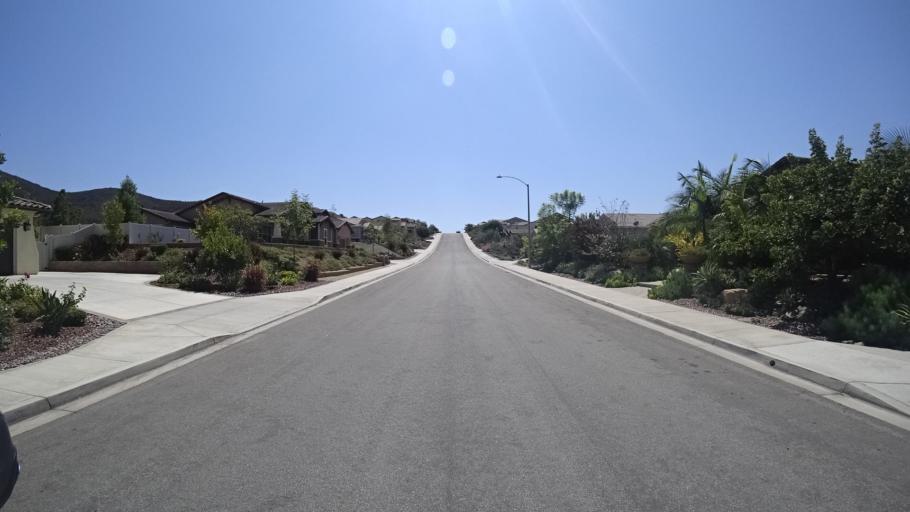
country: US
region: California
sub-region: San Diego County
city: San Marcos
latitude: 33.1824
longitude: -117.1937
